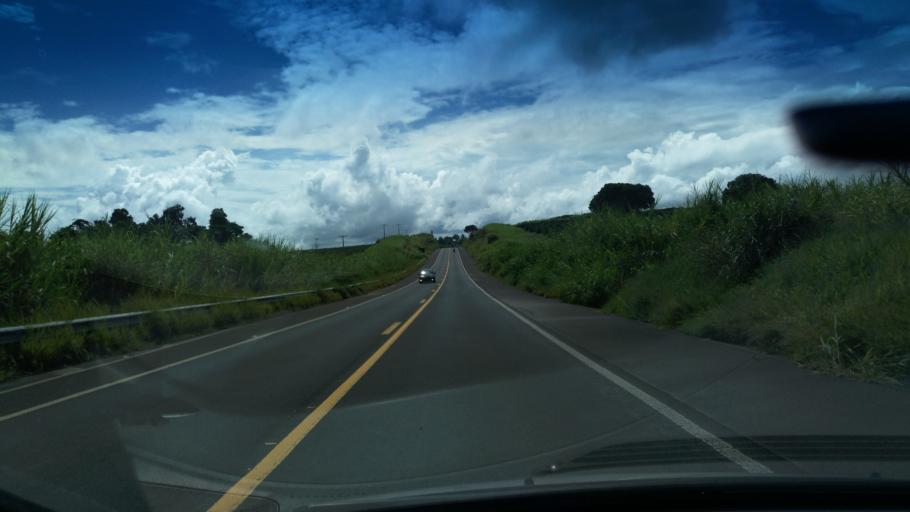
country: BR
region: Sao Paulo
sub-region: Santo Antonio Do Jardim
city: Espirito Santo do Pinhal
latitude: -22.1457
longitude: -46.7159
